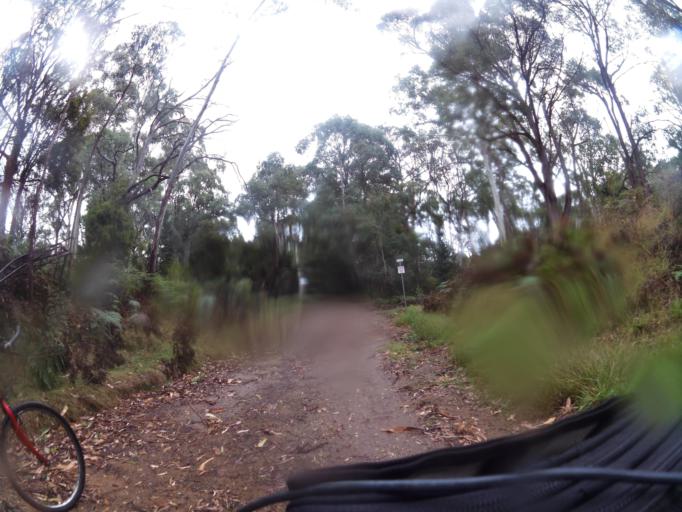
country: AU
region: New South Wales
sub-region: Greater Hume Shire
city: Holbrook
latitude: -36.1881
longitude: 147.5457
